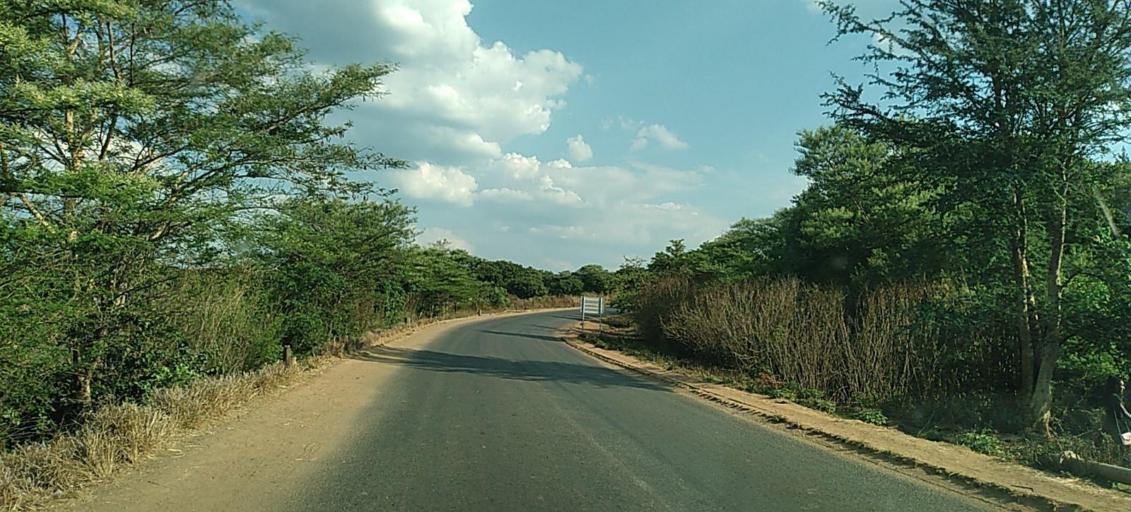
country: ZM
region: Copperbelt
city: Luanshya
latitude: -13.3468
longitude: 28.4203
